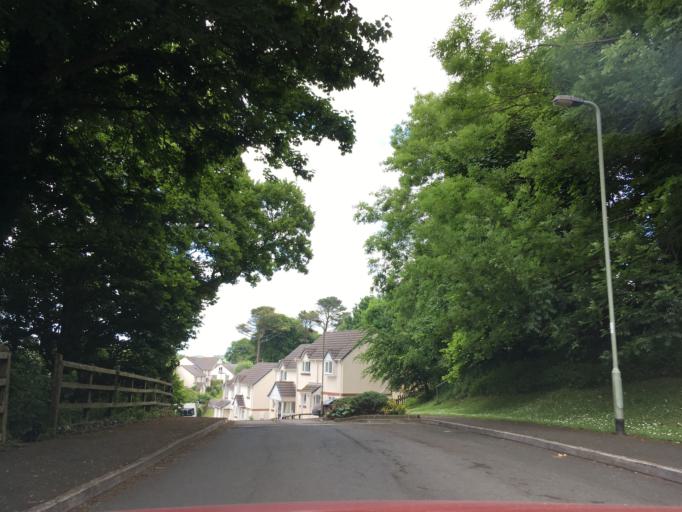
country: GB
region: England
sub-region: Devon
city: Dartmouth
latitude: 50.3551
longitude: -3.5915
